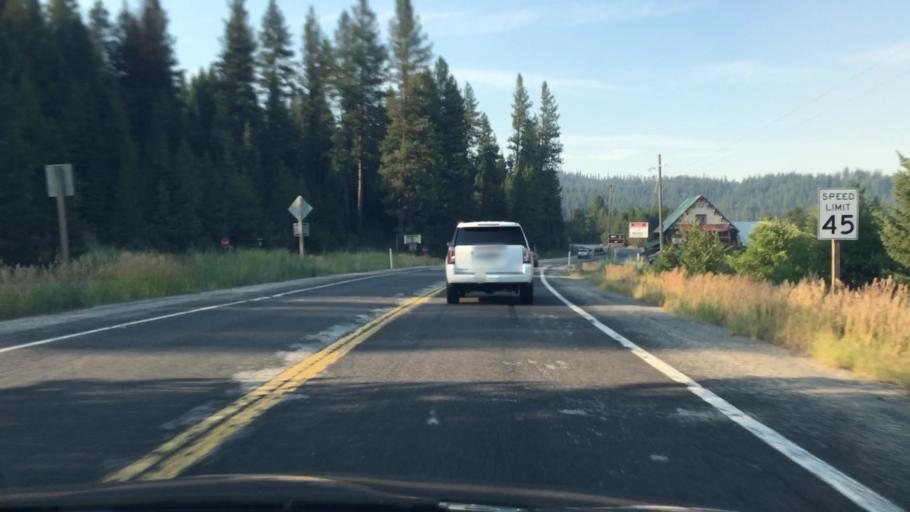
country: US
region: Idaho
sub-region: Valley County
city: Cascade
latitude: 44.3017
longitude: -116.0890
